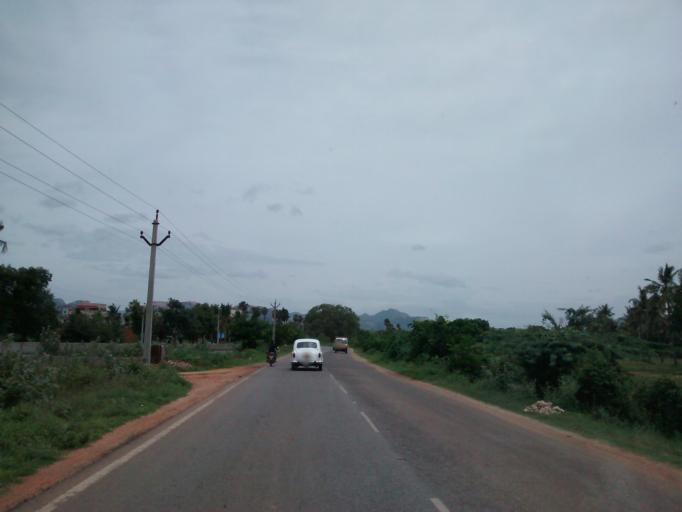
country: IN
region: Andhra Pradesh
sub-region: Chittoor
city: Narasingapuram
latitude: 13.6106
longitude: 79.3510
